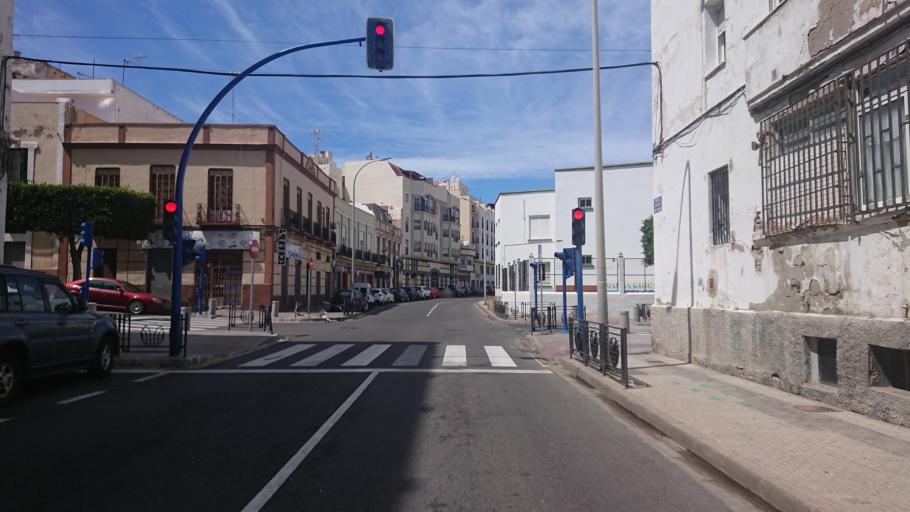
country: ES
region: Melilla
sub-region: Melilla
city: Melilla
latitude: 35.2844
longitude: -2.9415
